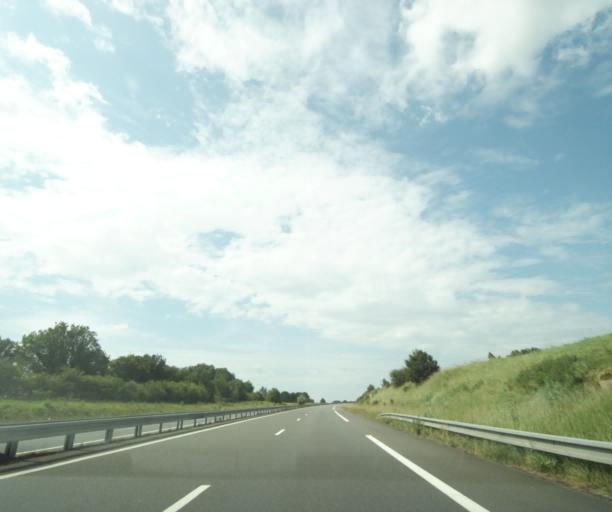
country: FR
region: Pays de la Loire
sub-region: Departement de Maine-et-Loire
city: Vivy
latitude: 47.3575
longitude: -0.0801
